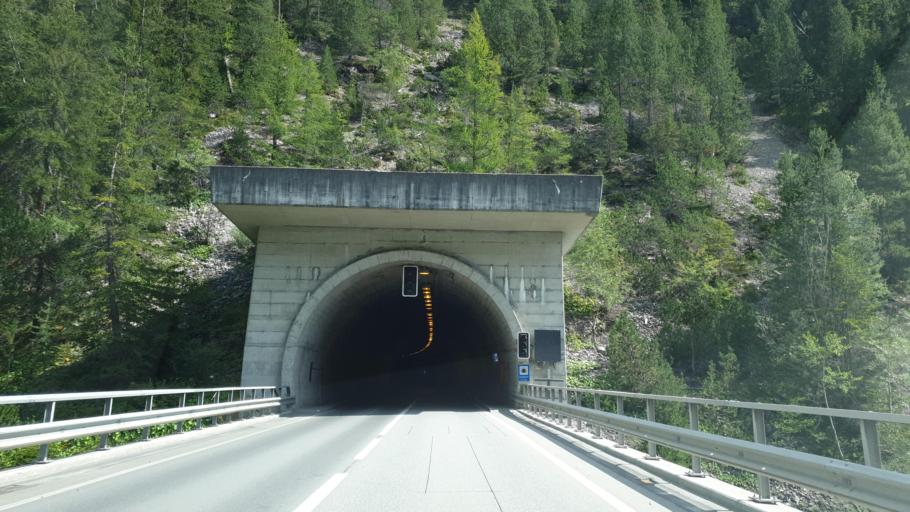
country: CH
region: Grisons
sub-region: Plessur District
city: Arosa
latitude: 46.7019
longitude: 9.7254
